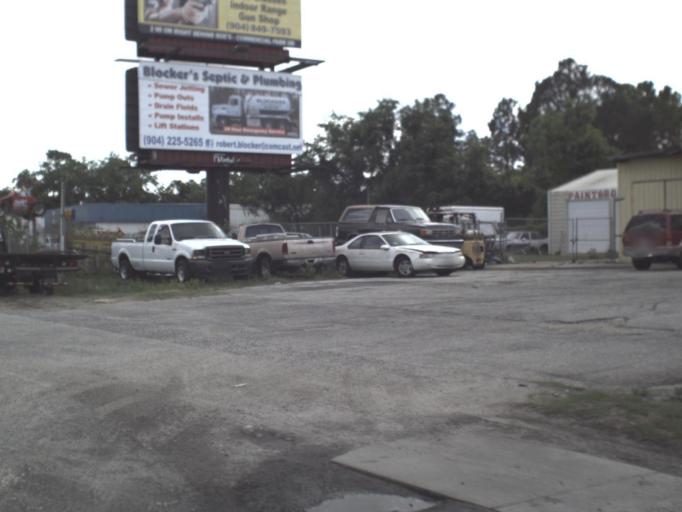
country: US
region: Florida
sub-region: Nassau County
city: Yulee
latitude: 30.6304
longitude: -81.6004
